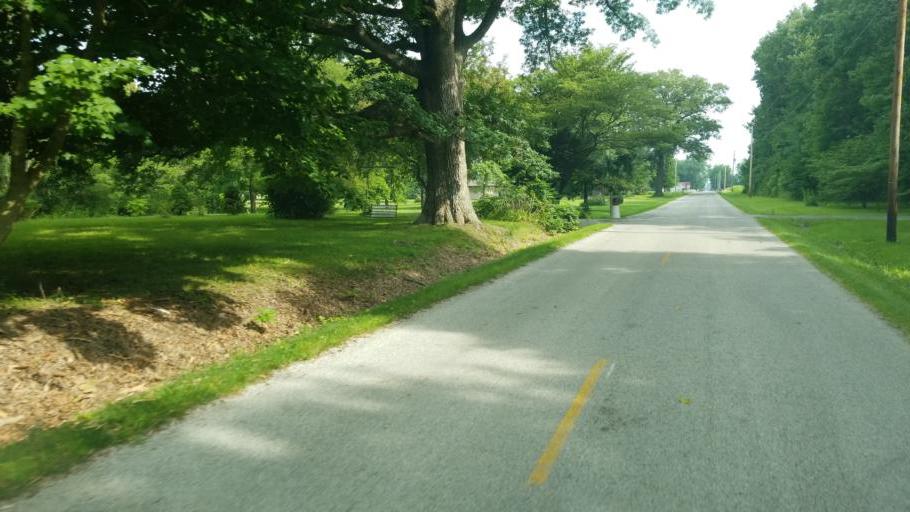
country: US
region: Ohio
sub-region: Marion County
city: Marion
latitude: 40.6370
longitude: -83.3049
